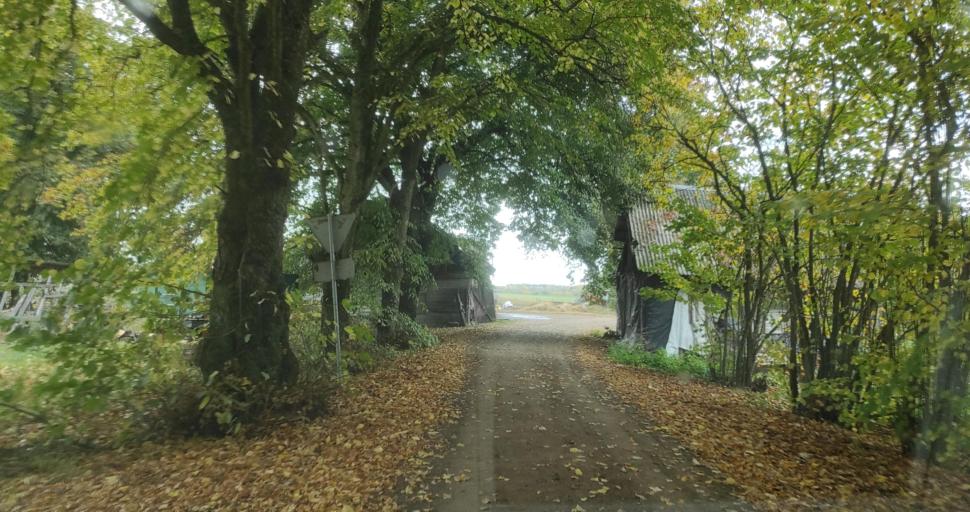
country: LV
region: Skrunda
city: Skrunda
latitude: 56.6980
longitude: 22.0072
